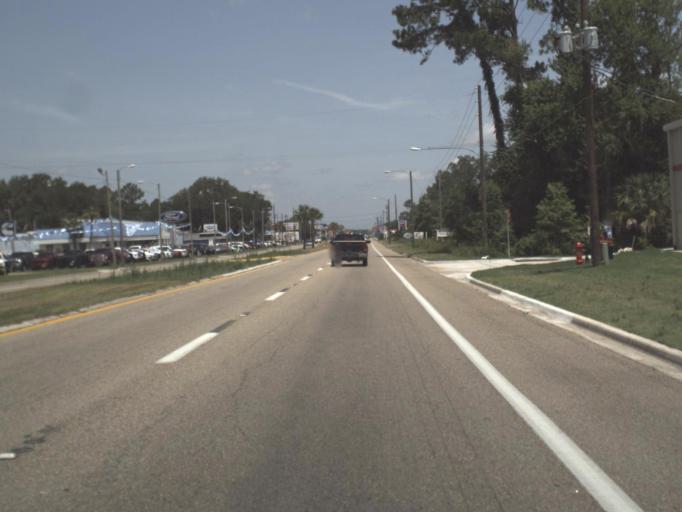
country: US
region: Florida
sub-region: Taylor County
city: Perry
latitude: 30.0887
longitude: -83.5733
